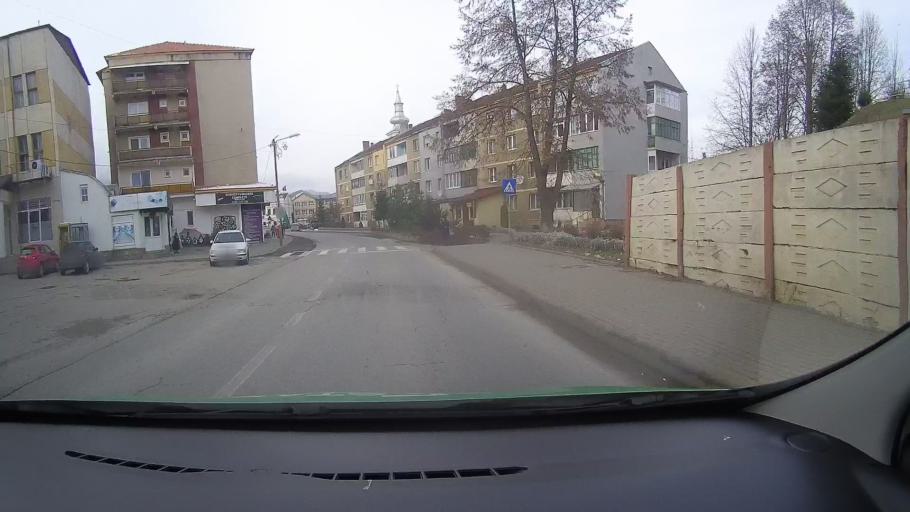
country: RO
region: Alba
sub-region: Oras Zlatna
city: Zlatna
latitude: 46.1105
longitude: 23.2257
